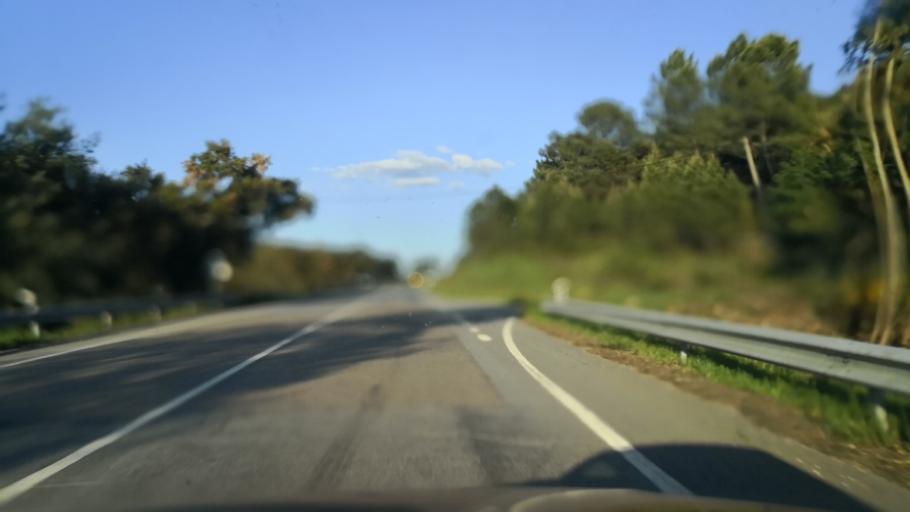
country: PT
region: Portalegre
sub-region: Marvao
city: Marvao
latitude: 39.3691
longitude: -7.3419
